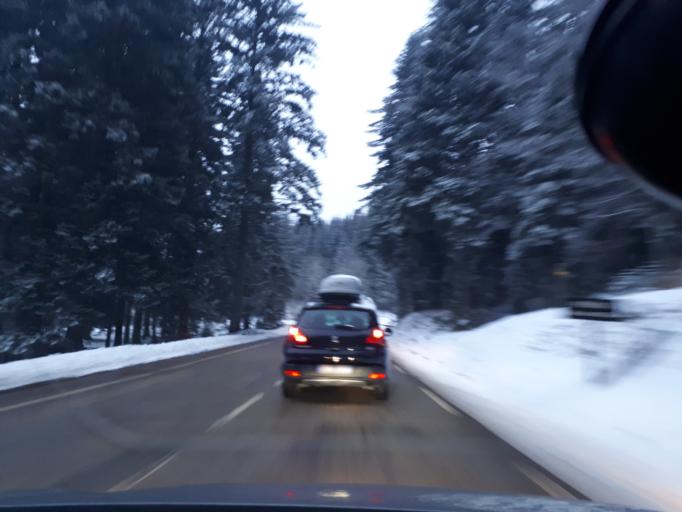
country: FR
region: Rhone-Alpes
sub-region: Departement de l'Isere
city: Vaulnaveys-le-Bas
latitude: 45.1014
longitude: 5.8482
